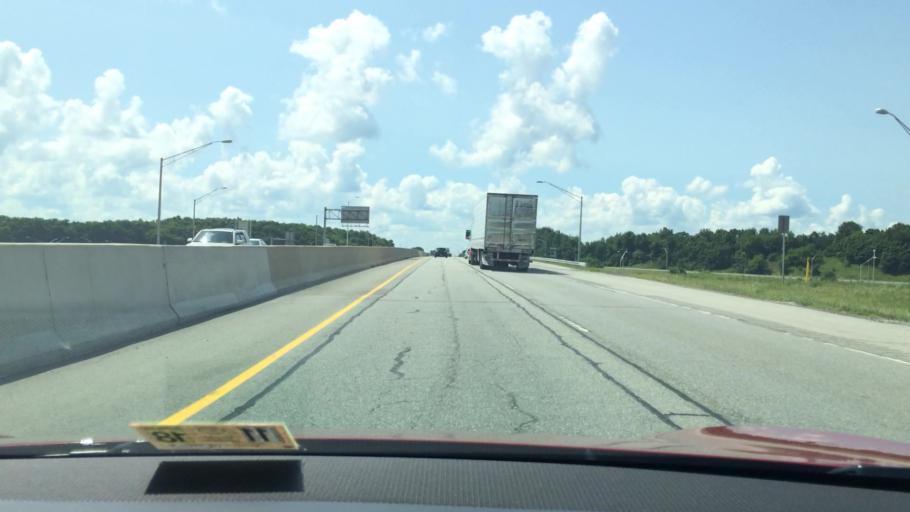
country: US
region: Indiana
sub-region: Saint Joseph County
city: South Bend
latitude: 41.7078
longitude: -86.3398
